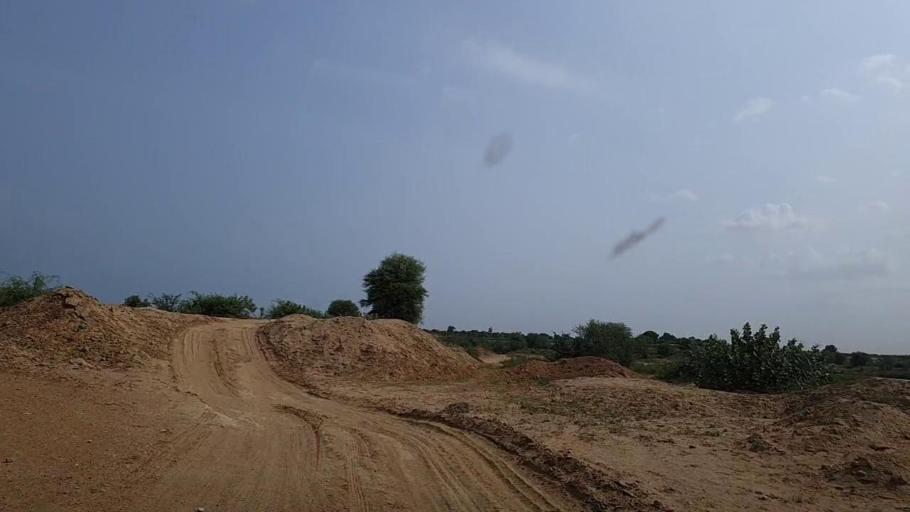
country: PK
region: Sindh
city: Kotri
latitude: 25.2601
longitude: 68.2622
